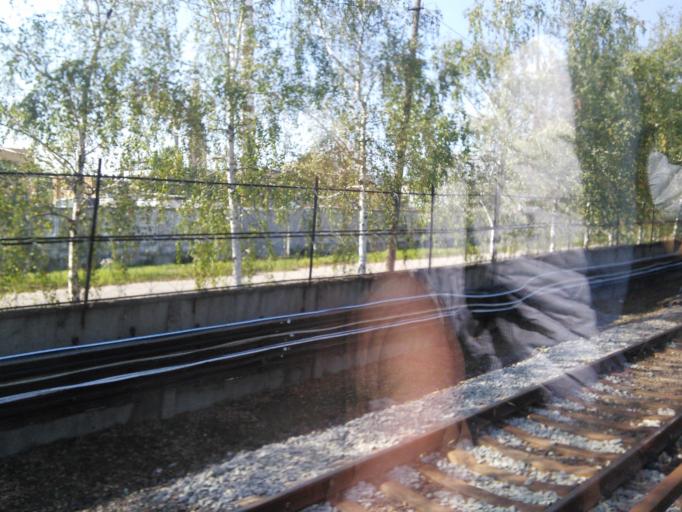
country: RU
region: Moskovskaya
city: Kozhukhovo
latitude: 55.6981
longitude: 37.6615
